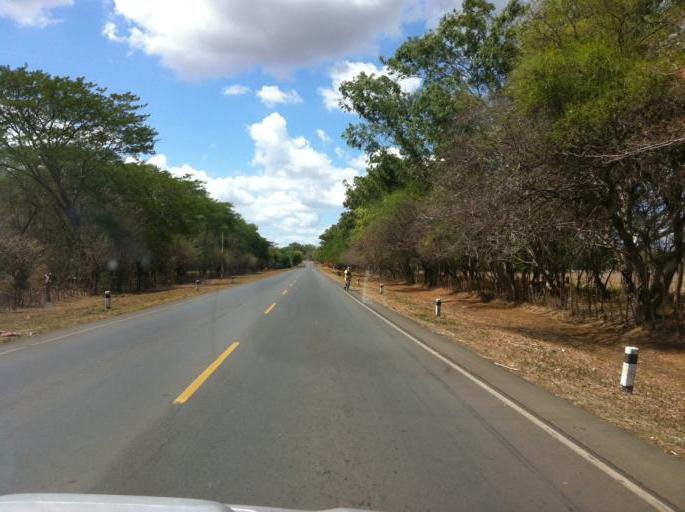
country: NI
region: Masaya
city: Nindiri
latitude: 12.0288
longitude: -86.1016
